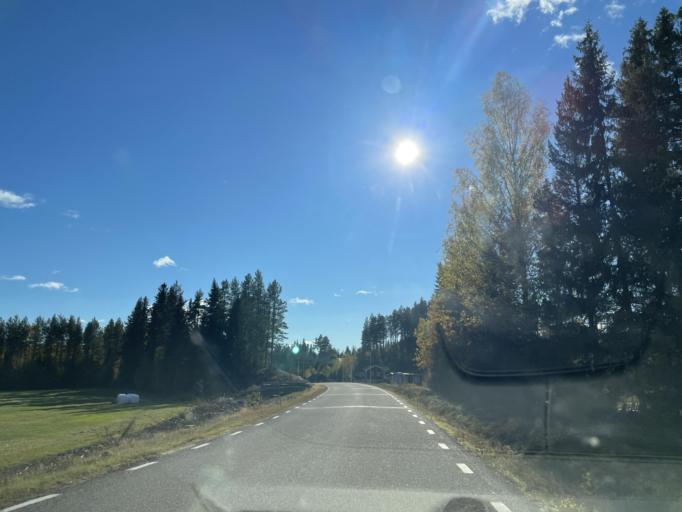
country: SE
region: Dalarna
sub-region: Malung-Saelens kommun
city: Malung
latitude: 60.8532
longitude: 13.4051
